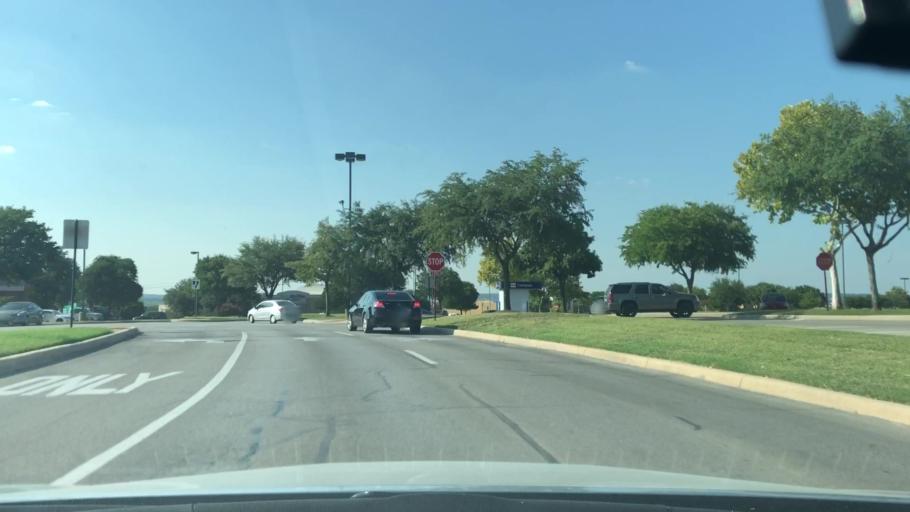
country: US
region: Texas
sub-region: Bexar County
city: Live Oak
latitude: 29.5726
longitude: -98.3240
